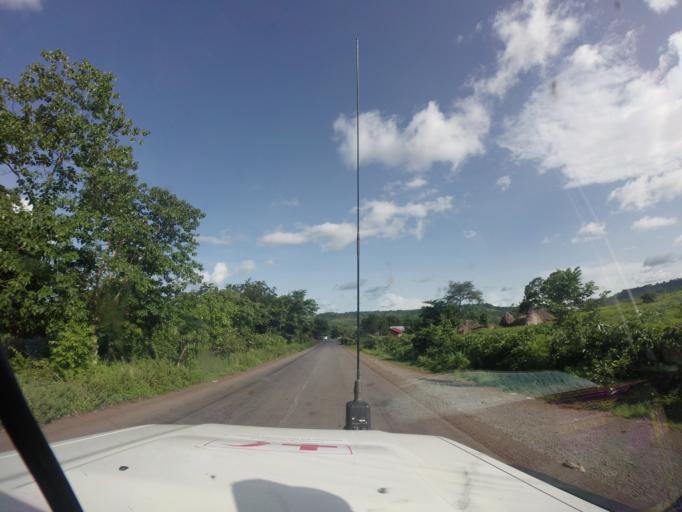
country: GN
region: Mamou
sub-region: Mamou Prefecture
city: Mamou
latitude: 10.1885
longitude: -12.4576
